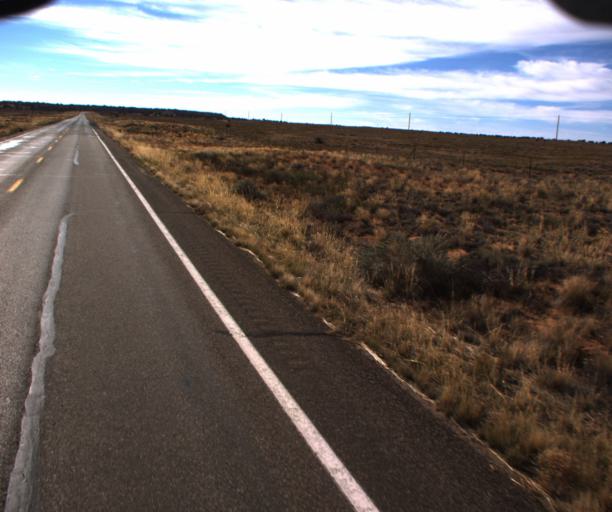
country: US
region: Arizona
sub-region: Coconino County
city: Kaibito
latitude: 36.6931
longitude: -111.2609
